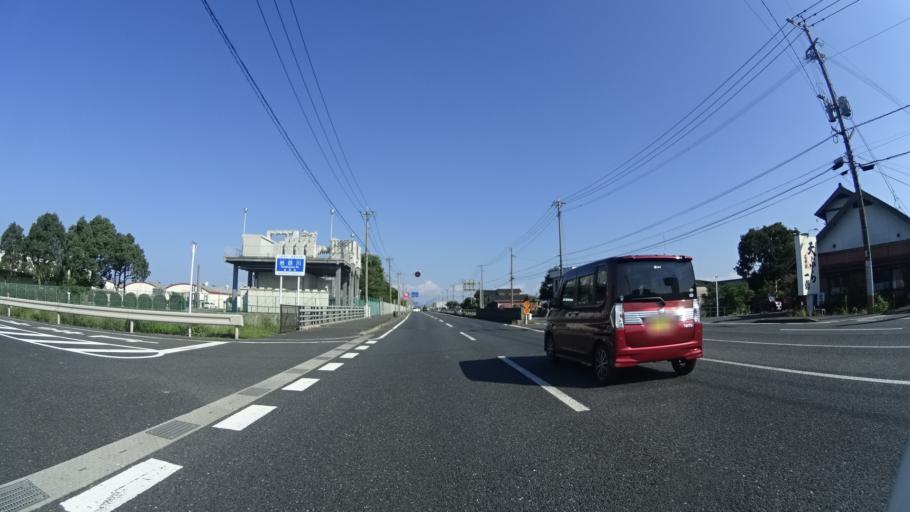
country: JP
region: Fukuoka
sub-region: Buzen-shi
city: Buzen
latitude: 33.5982
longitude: 131.1335
